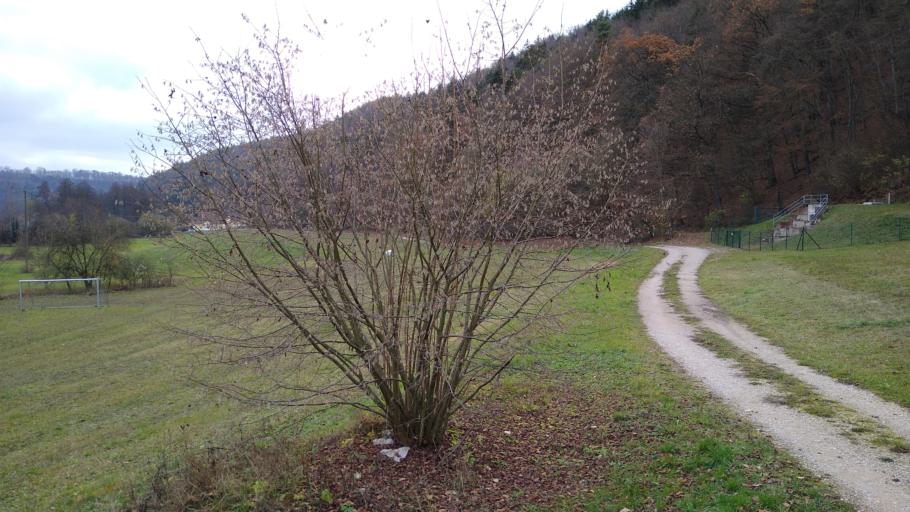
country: DE
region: Bavaria
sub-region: Upper Palatinate
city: Dietfurt
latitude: 49.0565
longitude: 11.6200
